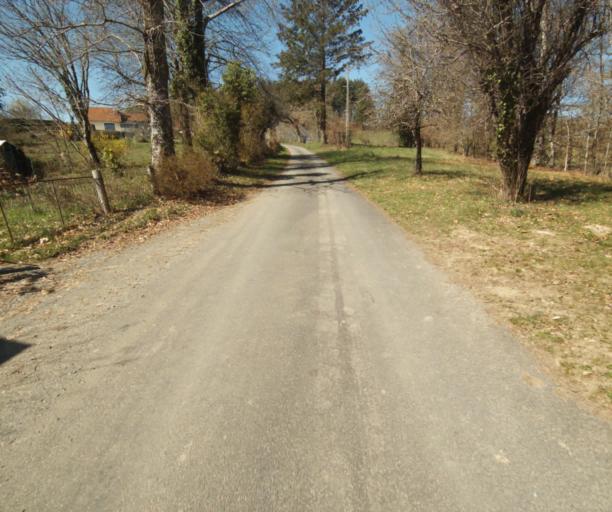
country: FR
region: Limousin
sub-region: Departement de la Correze
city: Saint-Mexant
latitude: 45.3041
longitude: 1.6242
